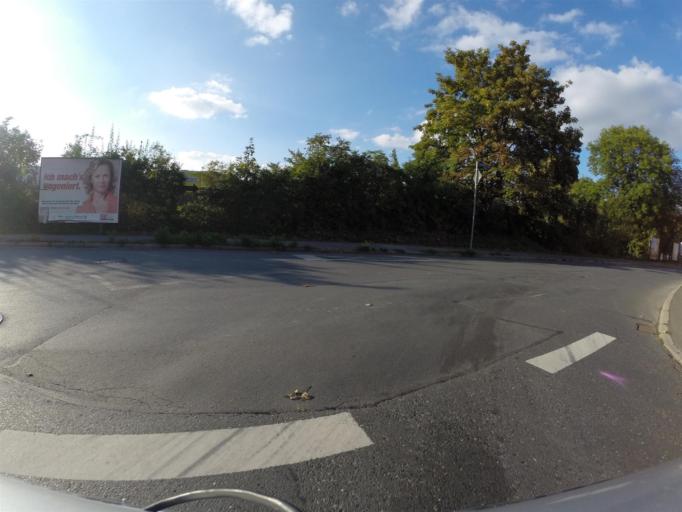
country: DE
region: Thuringia
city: Jena
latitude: 50.9376
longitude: 11.5958
